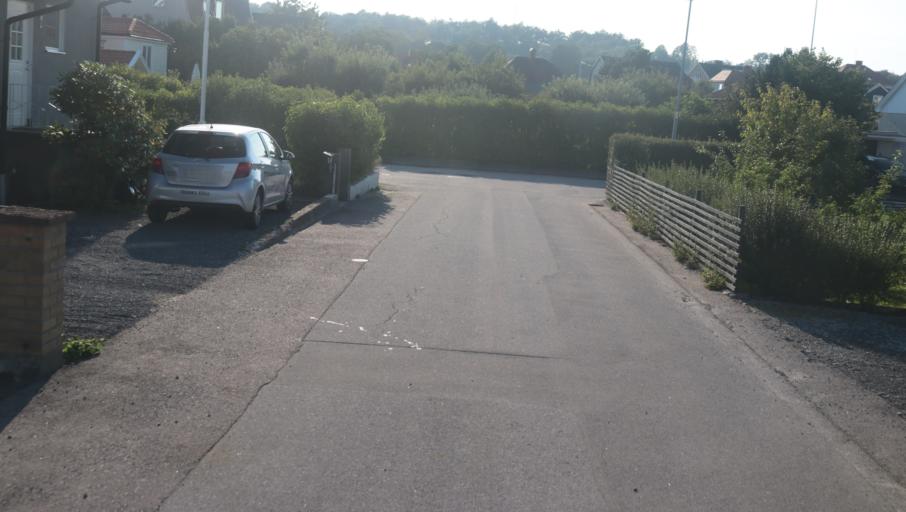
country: SE
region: Blekinge
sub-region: Karlshamns Kommun
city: Karlshamn
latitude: 56.1820
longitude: 14.8548
